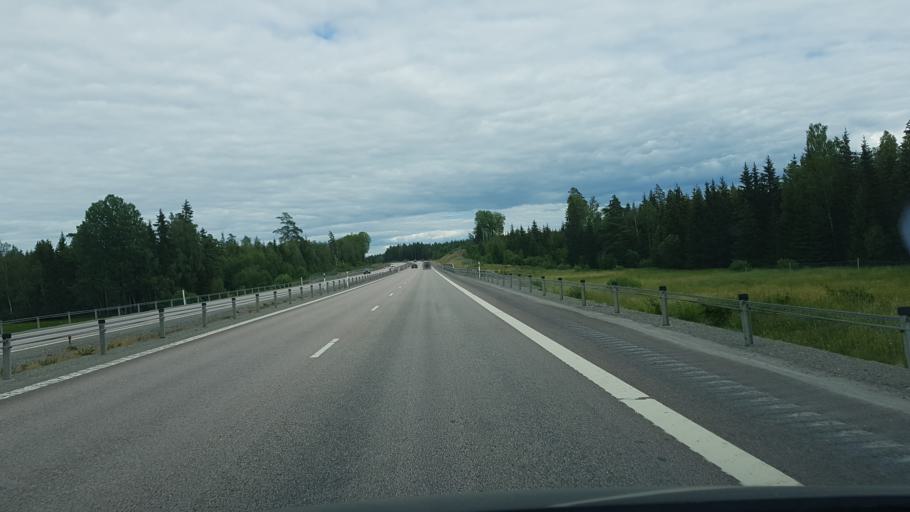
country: SE
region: Uppsala
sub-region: Enkopings Kommun
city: Hummelsta
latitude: 59.6394
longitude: 16.9276
